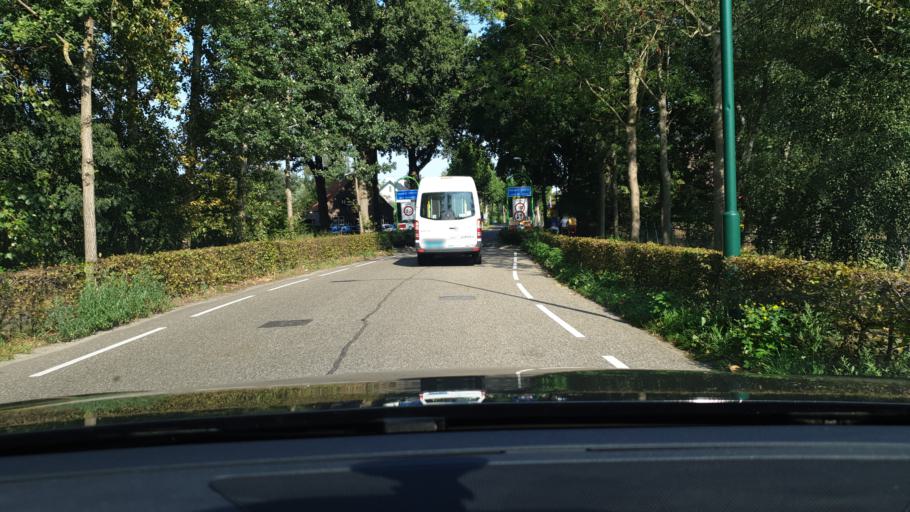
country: NL
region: North Brabant
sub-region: Gemeente Schijndel
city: Schijndel
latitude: 51.6487
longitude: 5.4643
